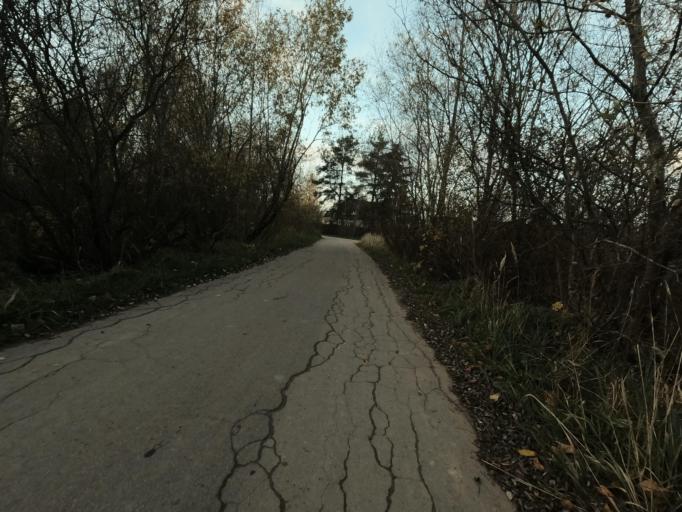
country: RU
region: Leningrad
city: Mga
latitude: 59.7752
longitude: 31.2121
